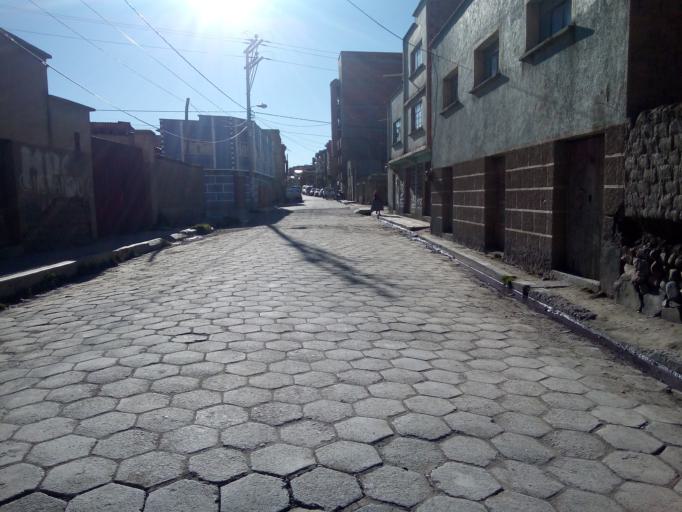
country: BO
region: La Paz
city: Achacachi
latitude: -16.0434
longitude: -68.6881
